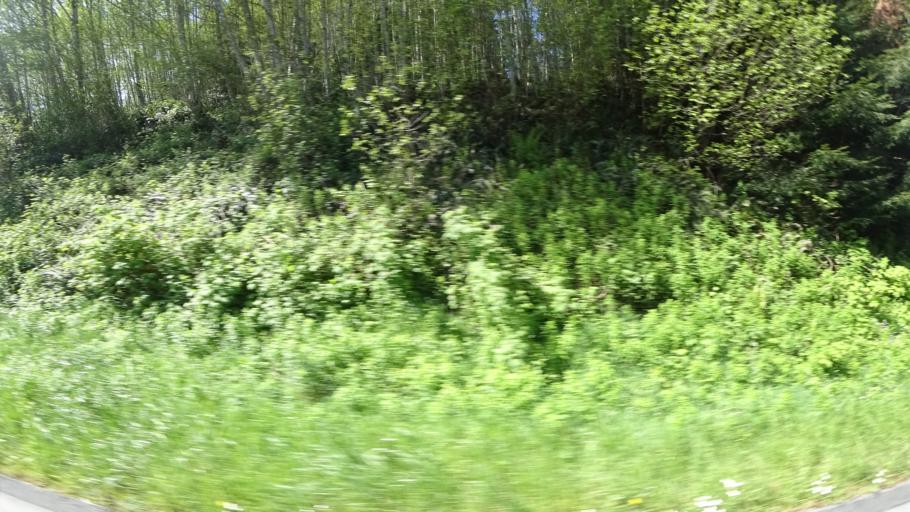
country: US
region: California
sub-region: Del Norte County
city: Bertsch-Oceanview
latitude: 41.4464
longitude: -124.0213
